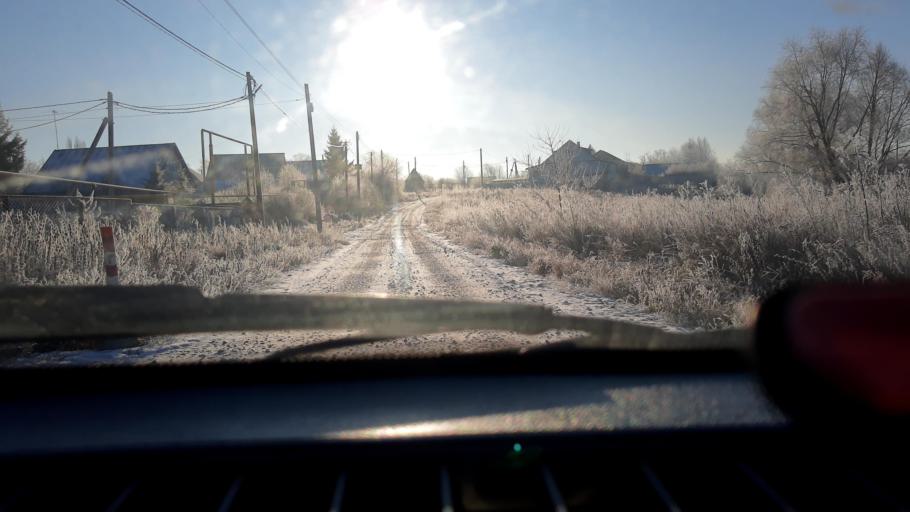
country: RU
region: Bashkortostan
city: Mikhaylovka
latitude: 54.8694
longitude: 55.7603
